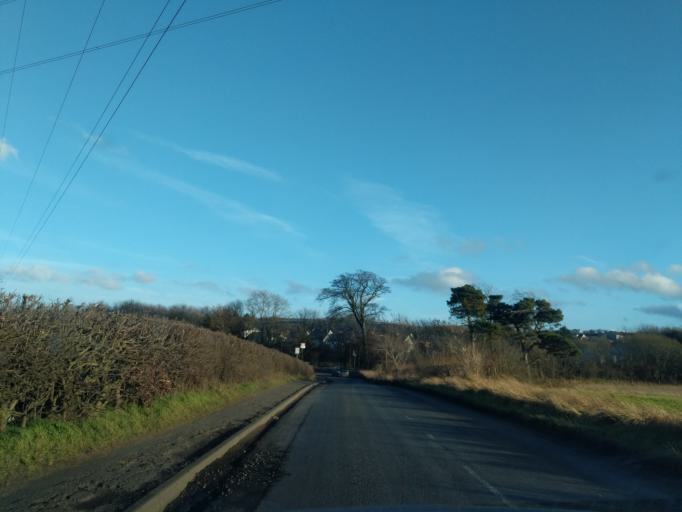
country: GB
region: Scotland
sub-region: Edinburgh
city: Currie
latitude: 55.9014
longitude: -3.3210
